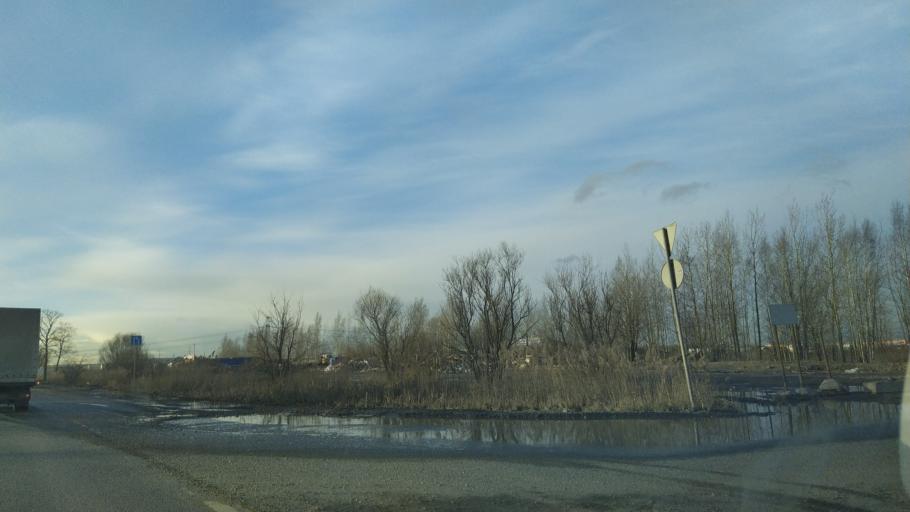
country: RU
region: St.-Petersburg
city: Petro-Slavyanka
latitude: 59.7763
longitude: 30.4456
